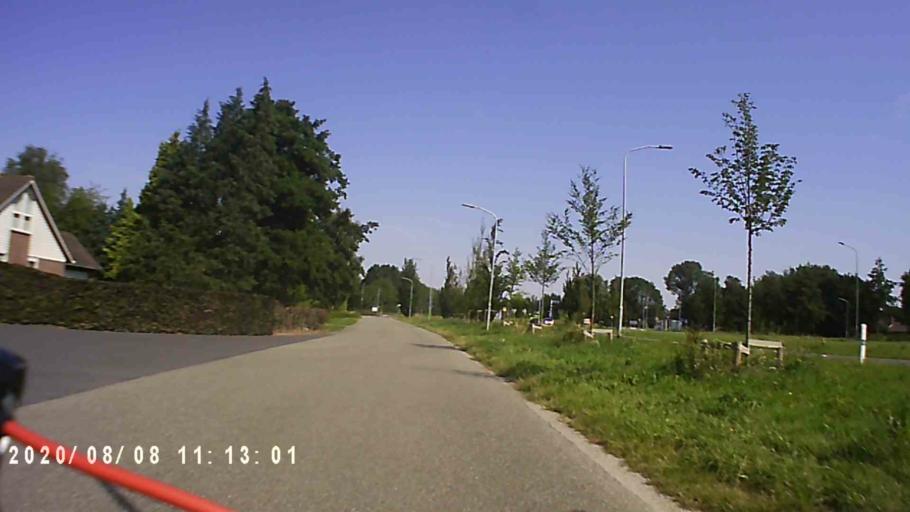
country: NL
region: Groningen
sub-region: Gemeente Leek
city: Leek
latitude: 53.1767
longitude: 6.3806
